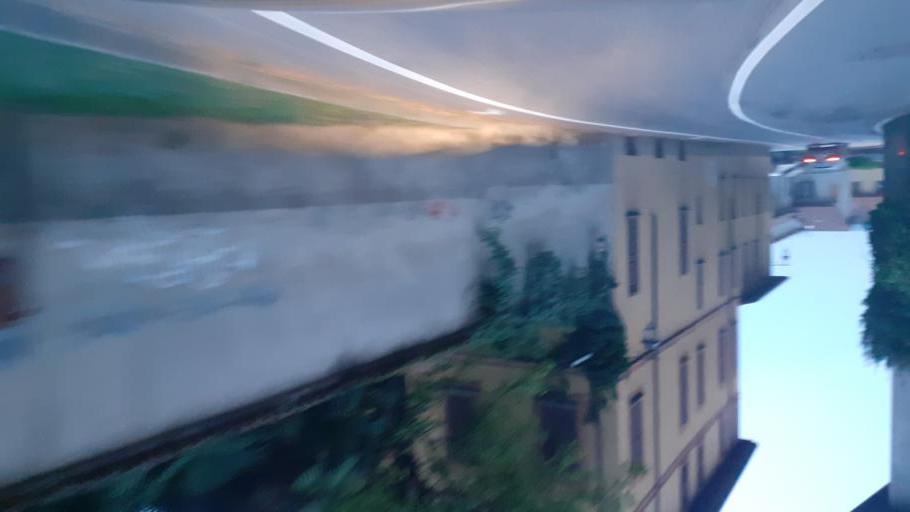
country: IT
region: Lombardy
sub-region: Provincia di Lecco
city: Bulciago
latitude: 45.7548
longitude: 9.2882
